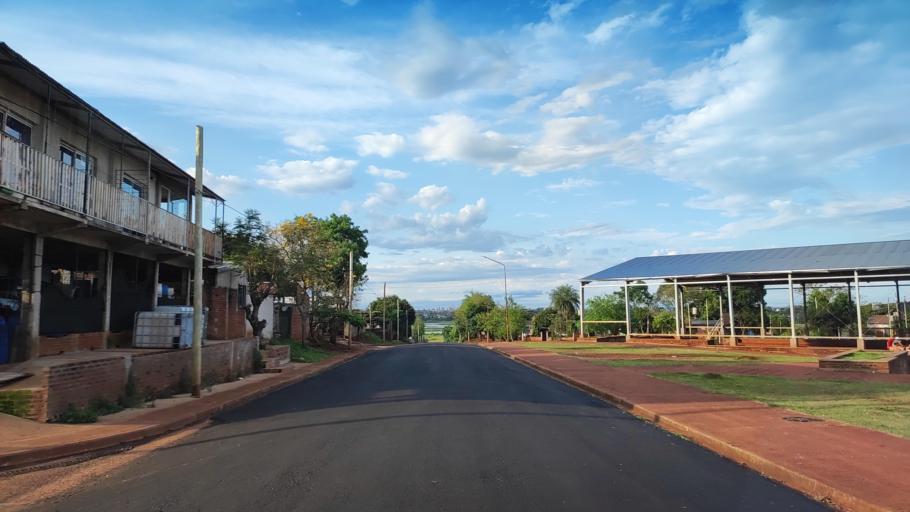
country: AR
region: Misiones
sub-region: Departamento de Capital
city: Posadas
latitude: -27.4357
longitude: -55.9073
